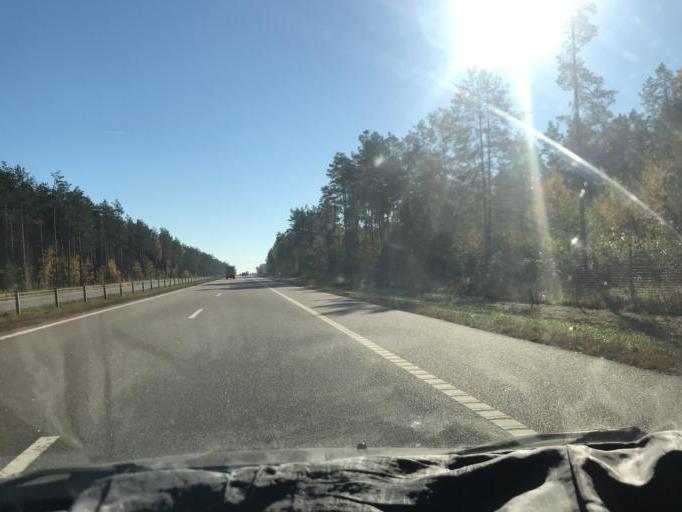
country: BY
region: Mogilev
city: Yalizava
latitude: 53.2630
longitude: 28.8919
